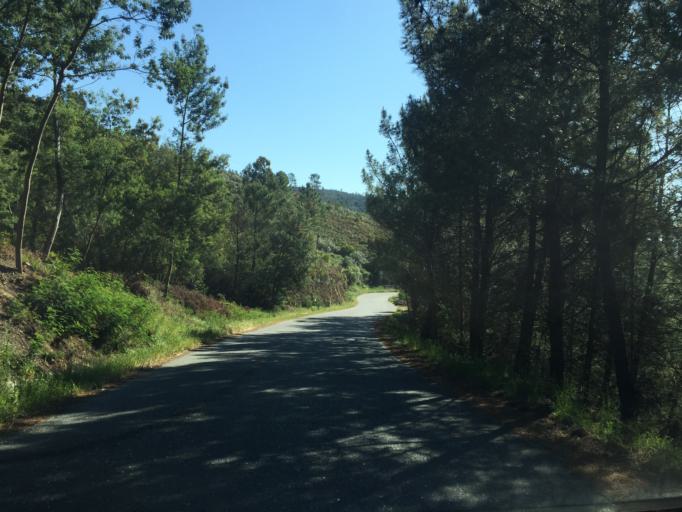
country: PT
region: Coimbra
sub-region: Pampilhosa da Serra
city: Pampilhosa da Serra
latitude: 40.0581
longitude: -7.8572
